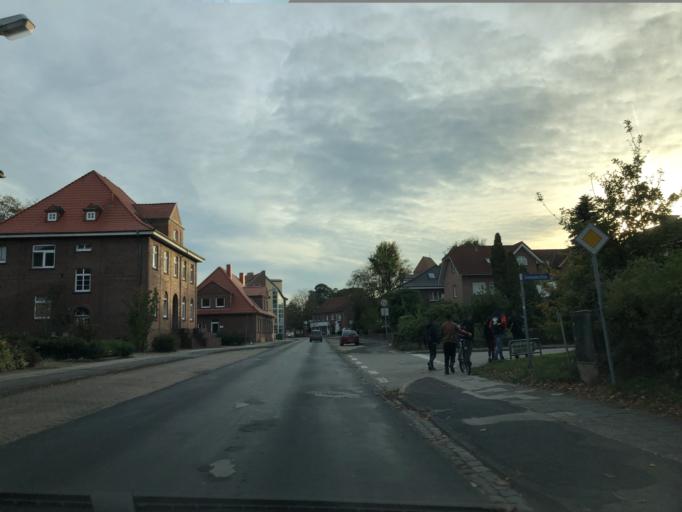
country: DE
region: Lower Saxony
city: Lehe
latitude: 53.0542
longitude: 7.3341
